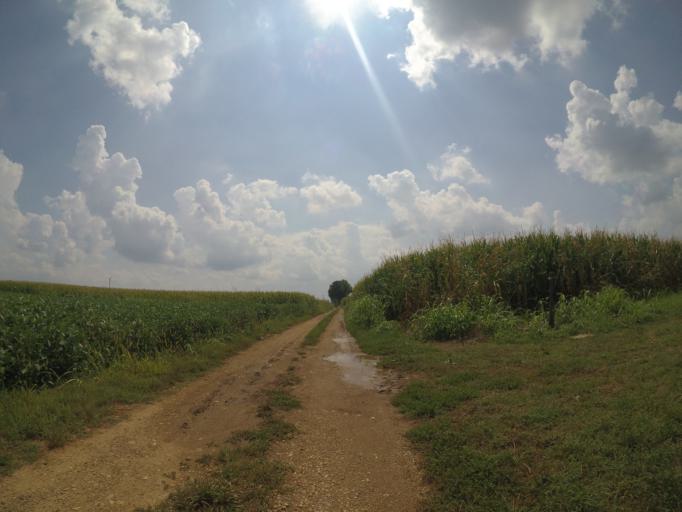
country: IT
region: Friuli Venezia Giulia
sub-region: Provincia di Udine
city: Bertiolo
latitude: 45.9680
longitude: 13.0480
